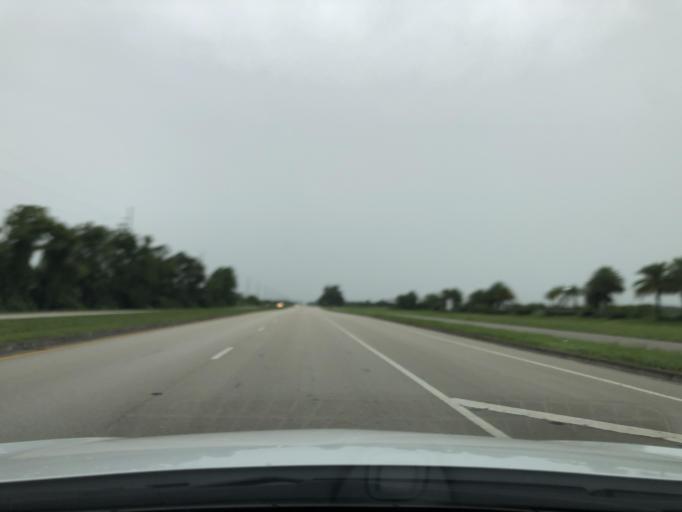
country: US
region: Florida
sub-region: Collier County
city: Immokalee
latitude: 26.2947
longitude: -81.4381
